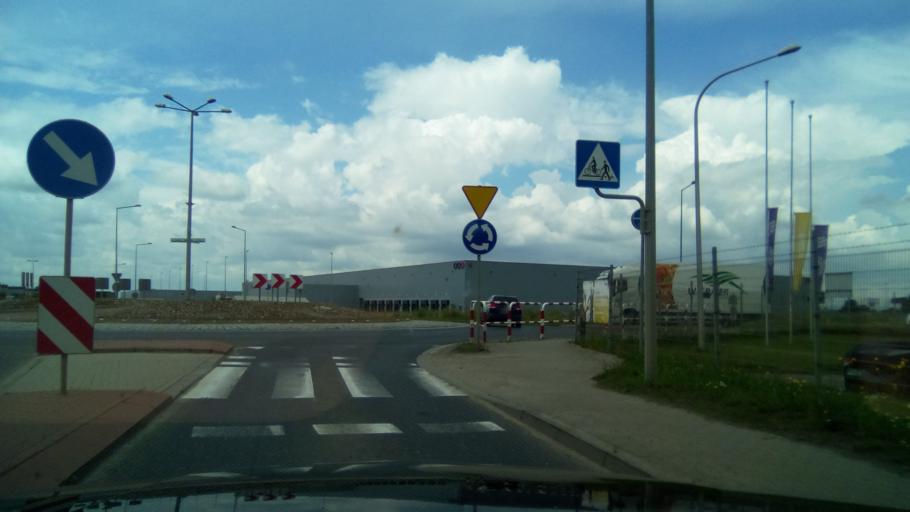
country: PL
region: Greater Poland Voivodeship
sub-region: Powiat poznanski
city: Komorniki
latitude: 52.3477
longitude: 16.8042
